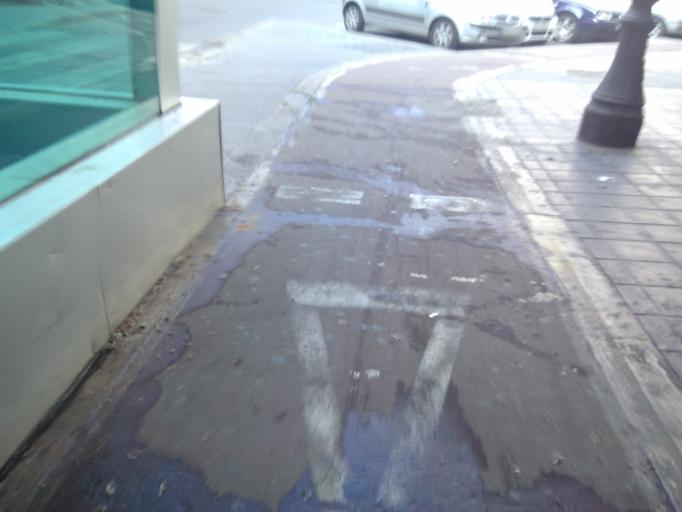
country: ES
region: Valencia
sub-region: Provincia de Valencia
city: Valencia
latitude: 39.4675
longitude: -0.3647
